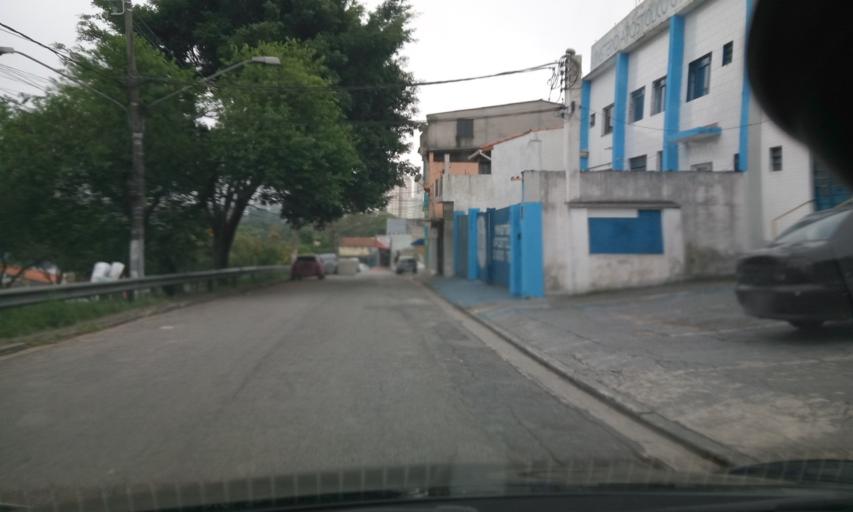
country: BR
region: Sao Paulo
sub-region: Sao Bernardo Do Campo
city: Sao Bernardo do Campo
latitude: -23.7022
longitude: -46.5627
